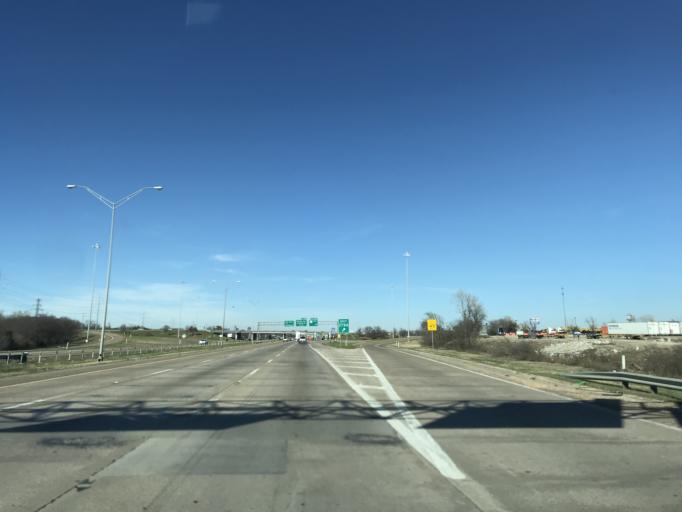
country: US
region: Texas
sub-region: Dallas County
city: Hutchins
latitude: 32.6963
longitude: -96.7510
